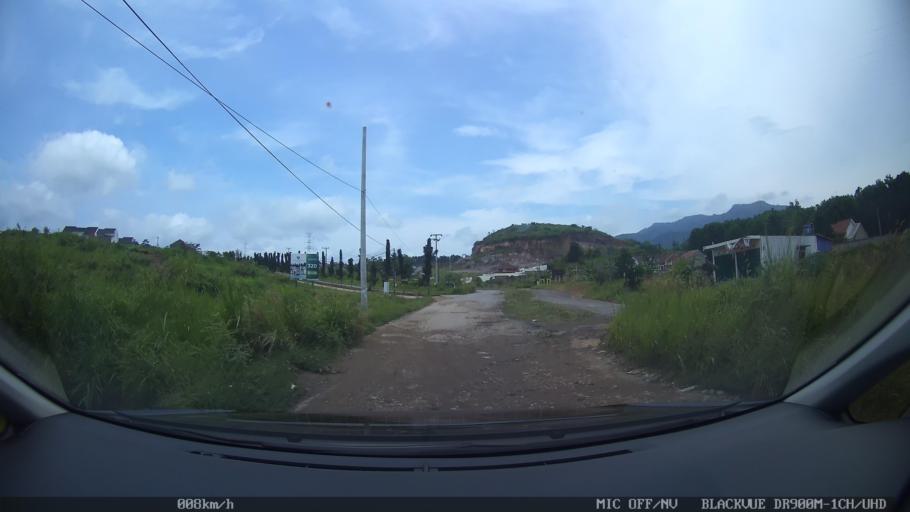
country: ID
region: Lampung
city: Bandarlampung
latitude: -5.4083
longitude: 105.1984
